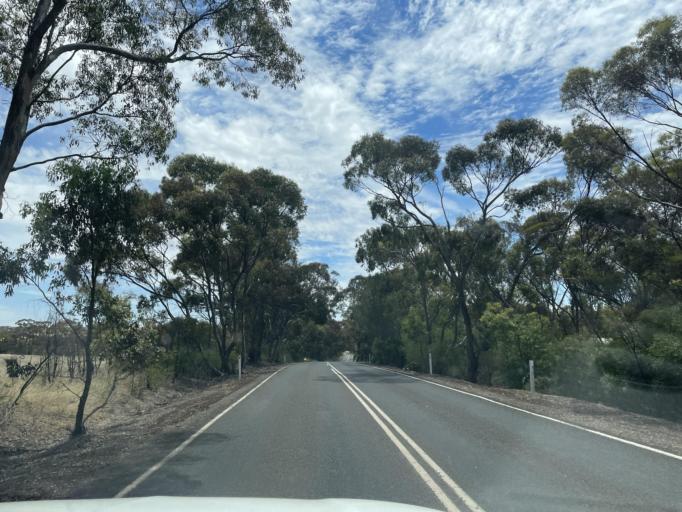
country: AU
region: South Australia
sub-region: Clare and Gilbert Valleys
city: Clare
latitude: -33.9008
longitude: 138.6904
